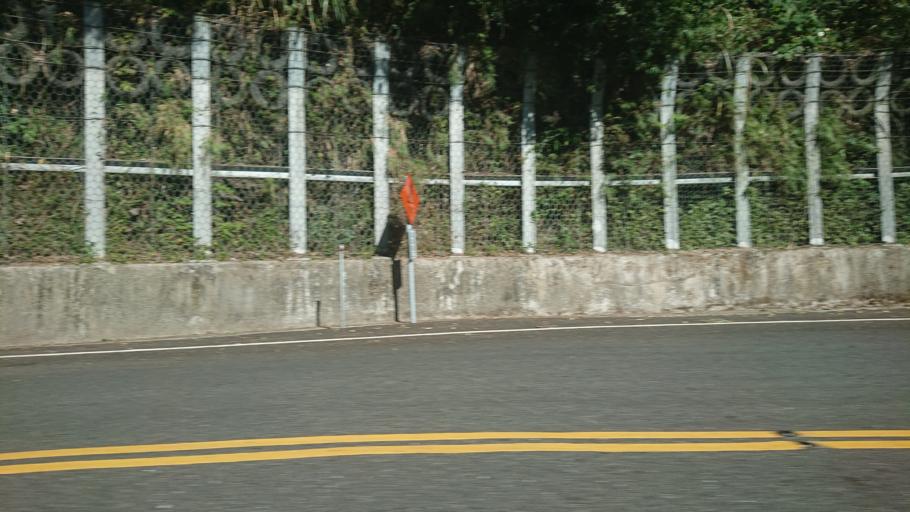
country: TW
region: Taiwan
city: Lugu
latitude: 23.4759
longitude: 120.7338
